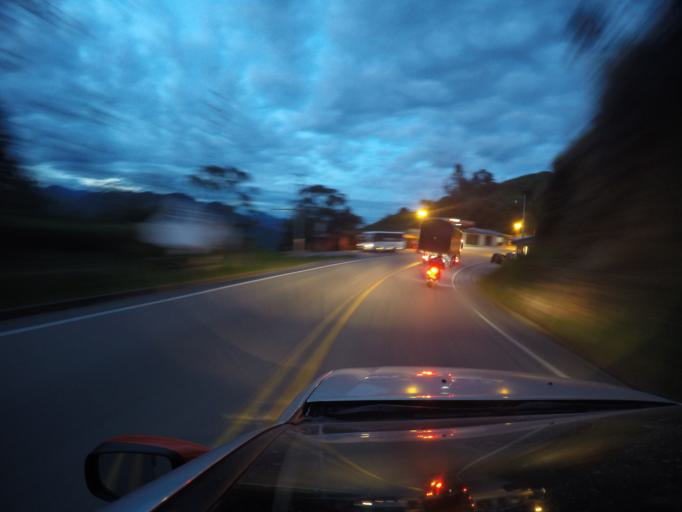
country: CO
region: Tolima
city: Casabianca
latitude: 5.1396
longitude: -75.1285
